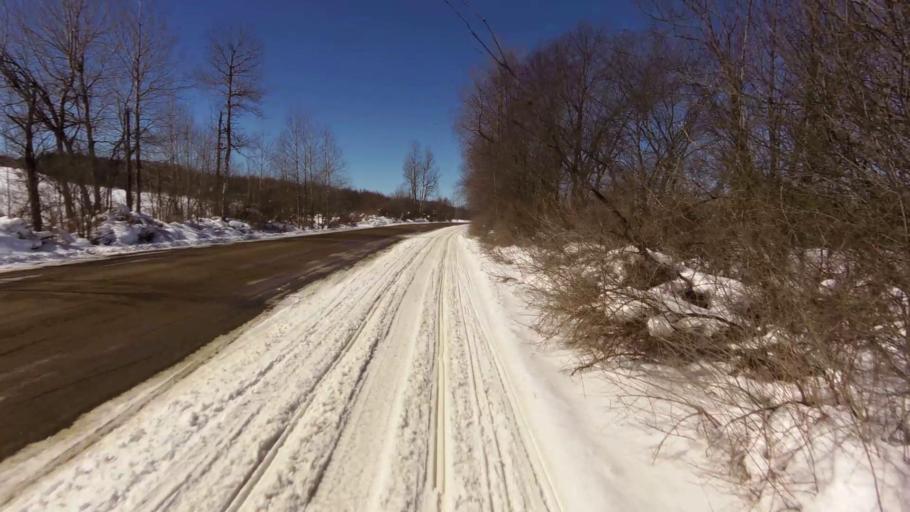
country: US
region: New York
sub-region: Cattaraugus County
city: Delevan
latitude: 42.4348
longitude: -78.4068
